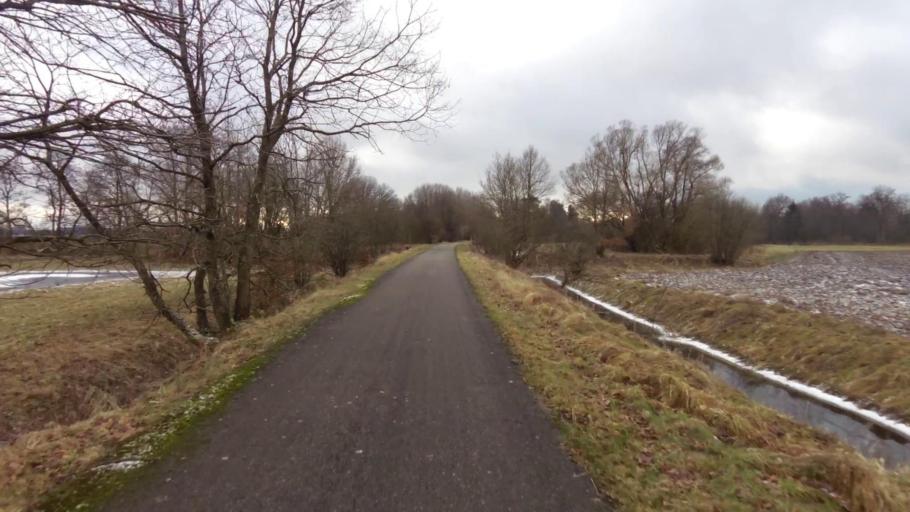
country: PL
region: West Pomeranian Voivodeship
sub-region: Powiat drawski
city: Zlocieniec
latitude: 53.6220
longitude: 16.0567
